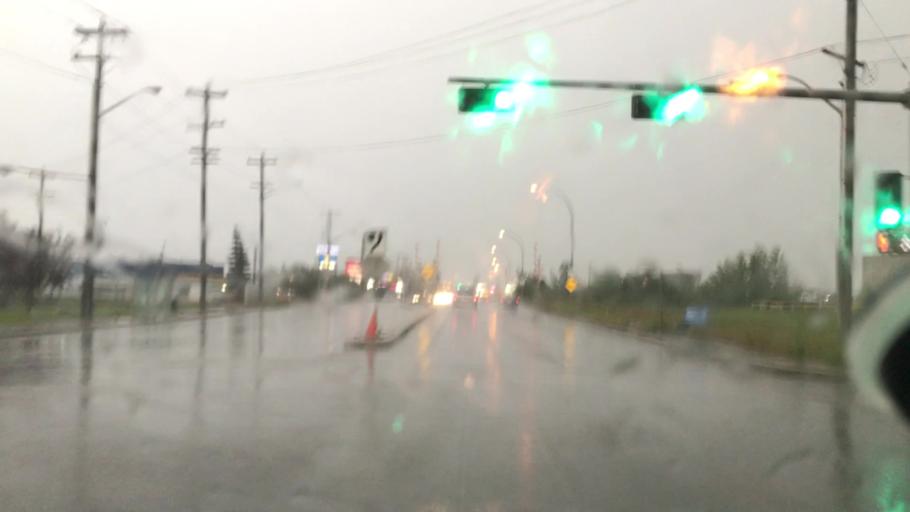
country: CA
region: Alberta
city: Edmonton
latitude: 53.5050
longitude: -113.4427
